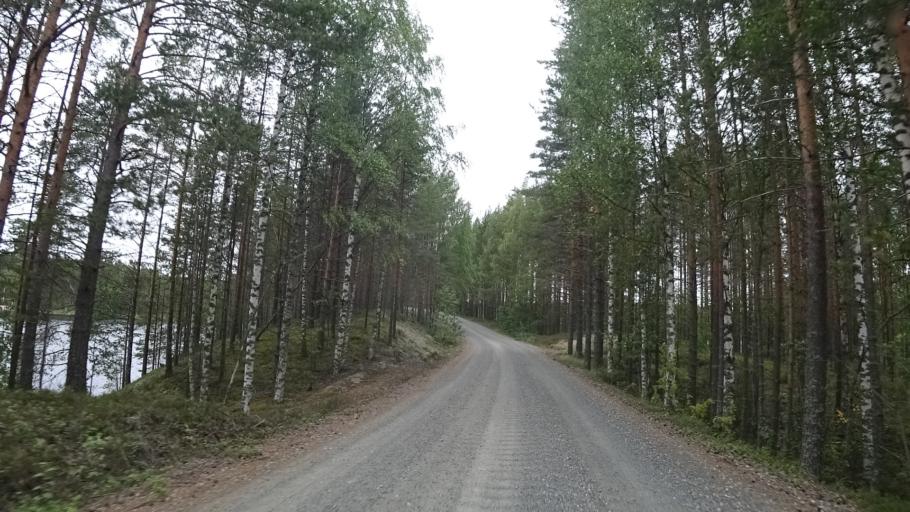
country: FI
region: North Karelia
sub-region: Joensuu
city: Ilomantsi
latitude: 62.6173
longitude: 31.1956
